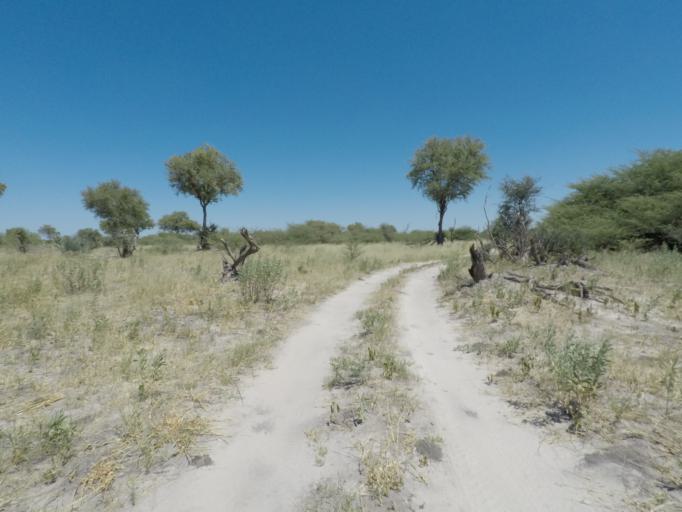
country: BW
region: North West
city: Maun
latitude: -19.4492
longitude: 23.5565
